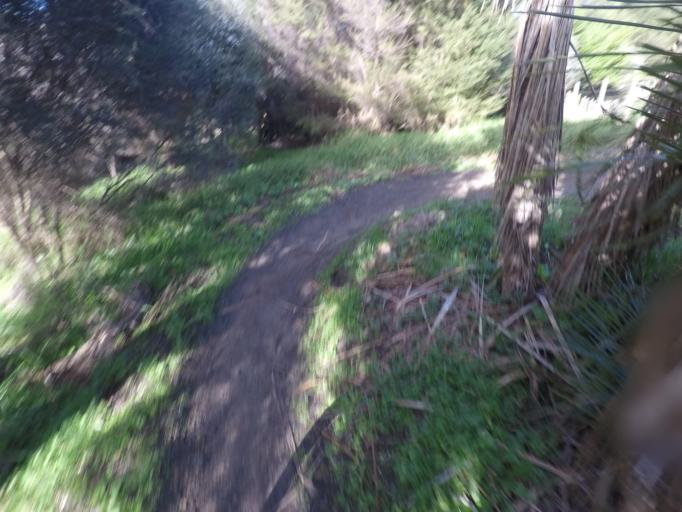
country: NZ
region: Auckland
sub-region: Auckland
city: Manukau City
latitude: -36.9912
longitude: 174.9068
